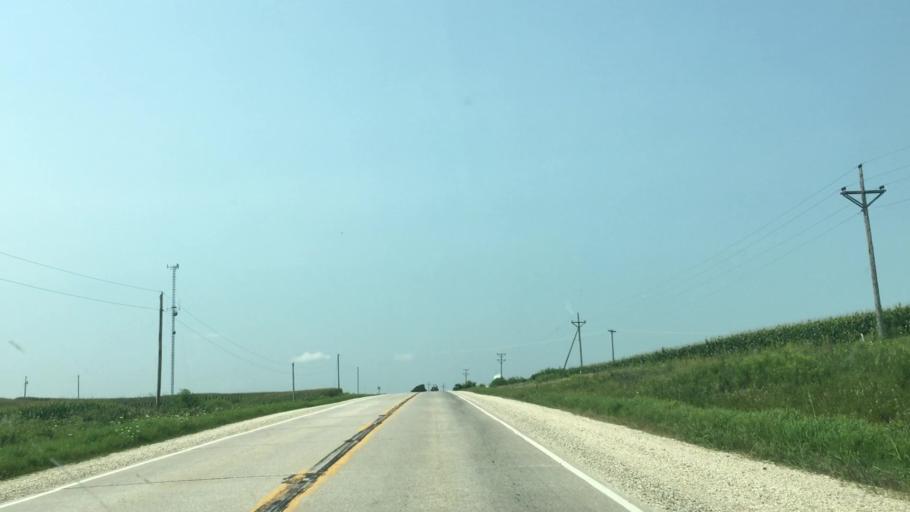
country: US
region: Iowa
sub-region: Fayette County
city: West Union
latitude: 43.0882
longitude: -91.8512
